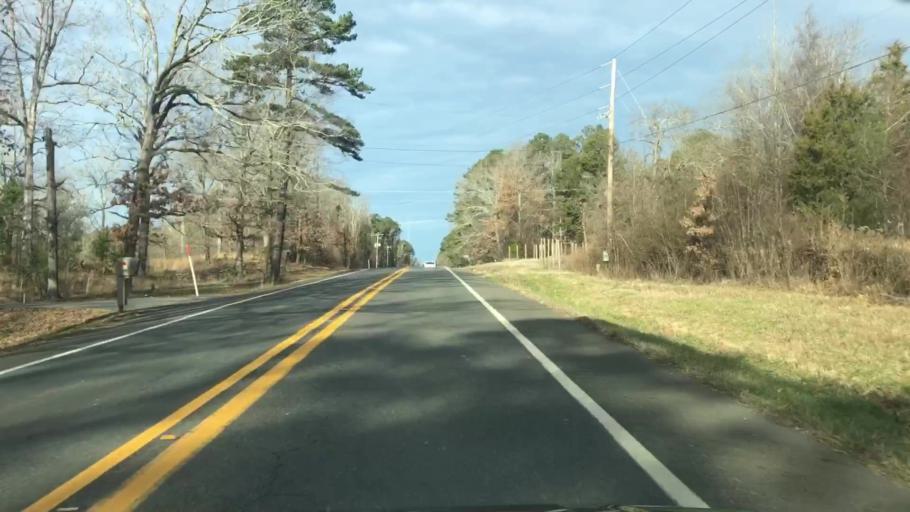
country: US
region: Arkansas
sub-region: Montgomery County
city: Mount Ida
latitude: 34.5402
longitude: -93.6055
